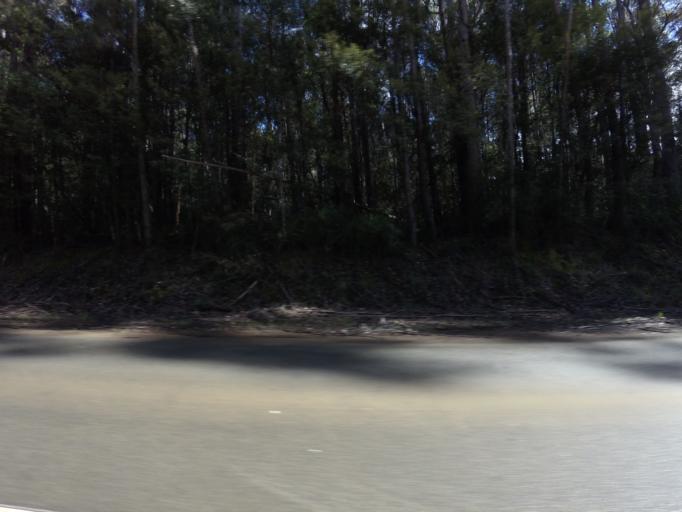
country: AU
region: Tasmania
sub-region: Huon Valley
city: Geeveston
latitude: -43.3423
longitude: 146.9650
